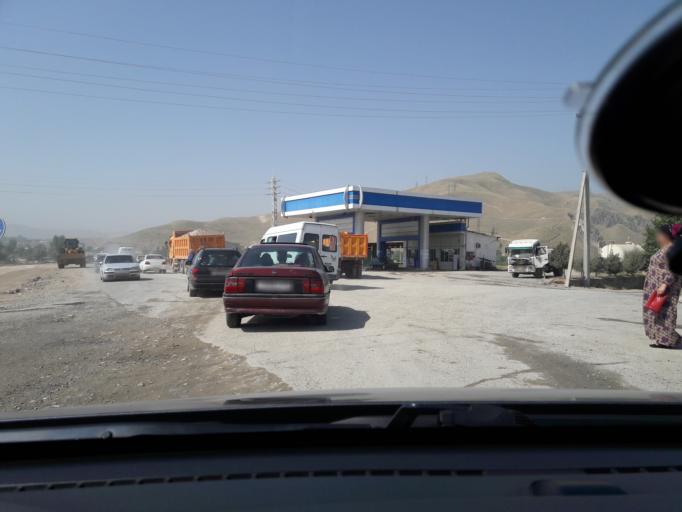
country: TJ
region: Dushanbe
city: Boshkengash
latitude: 38.4533
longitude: 68.7353
